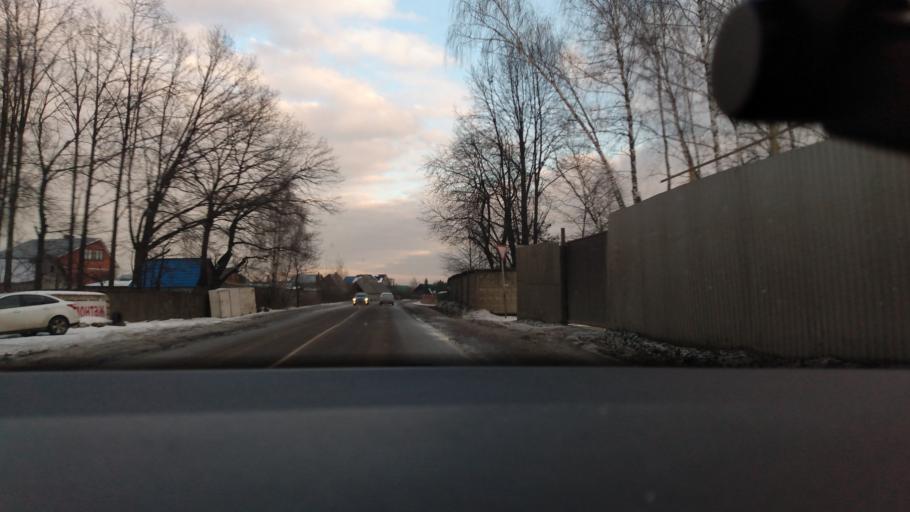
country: RU
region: Moskovskaya
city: Rodniki
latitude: 55.6953
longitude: 38.0640
